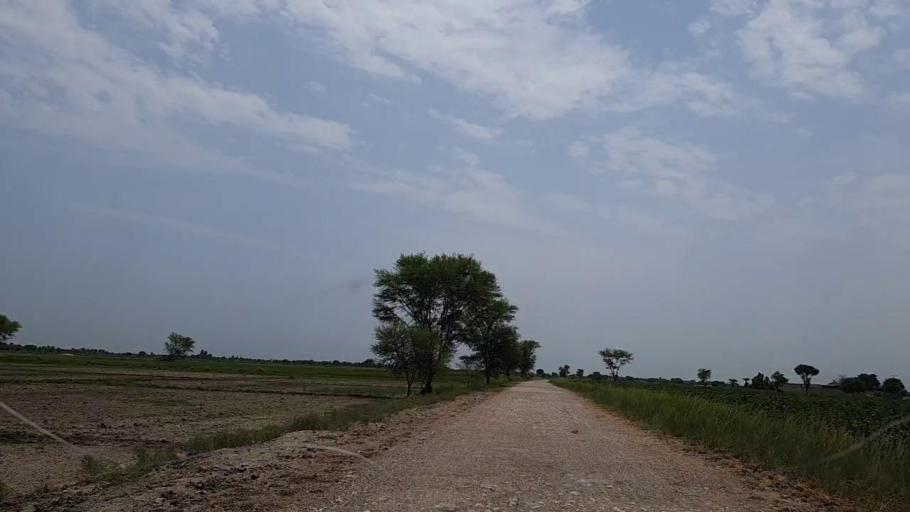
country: PK
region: Sindh
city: Tharu Shah
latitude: 26.9170
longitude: 68.0813
